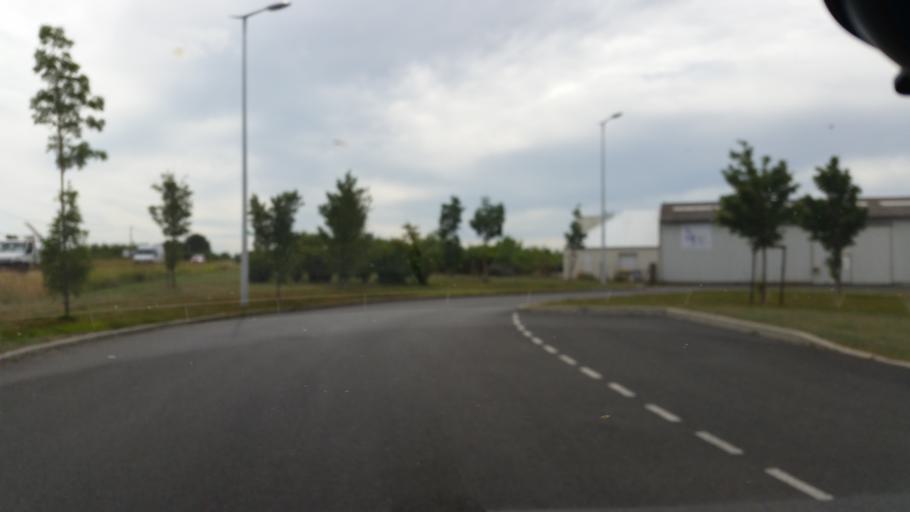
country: FR
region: Poitou-Charentes
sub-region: Departement de la Charente-Maritime
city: Surgeres
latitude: 46.1081
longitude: -0.7790
